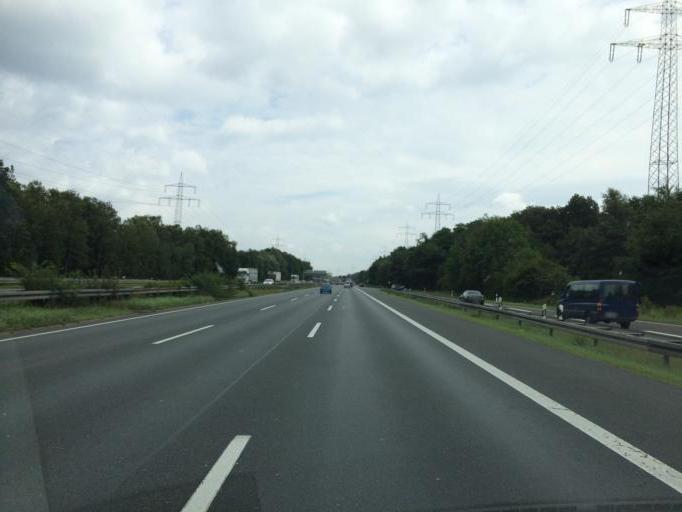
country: DE
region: Lower Saxony
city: Isernhagen Farster Bauerschaft
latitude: 52.4103
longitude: 9.8517
